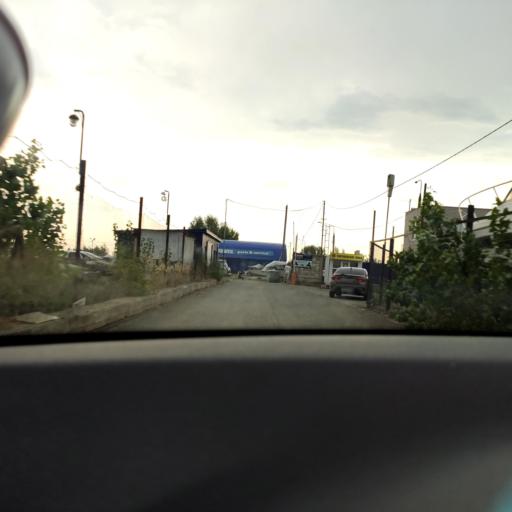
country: RU
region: Samara
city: Samara
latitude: 53.1752
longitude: 50.1232
